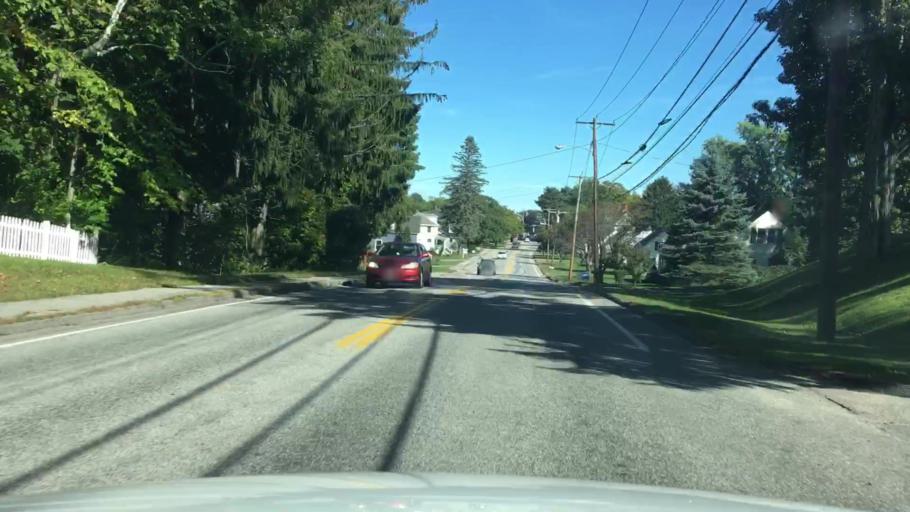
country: US
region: Maine
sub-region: Cumberland County
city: Westbrook
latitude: 43.6771
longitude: -70.3776
